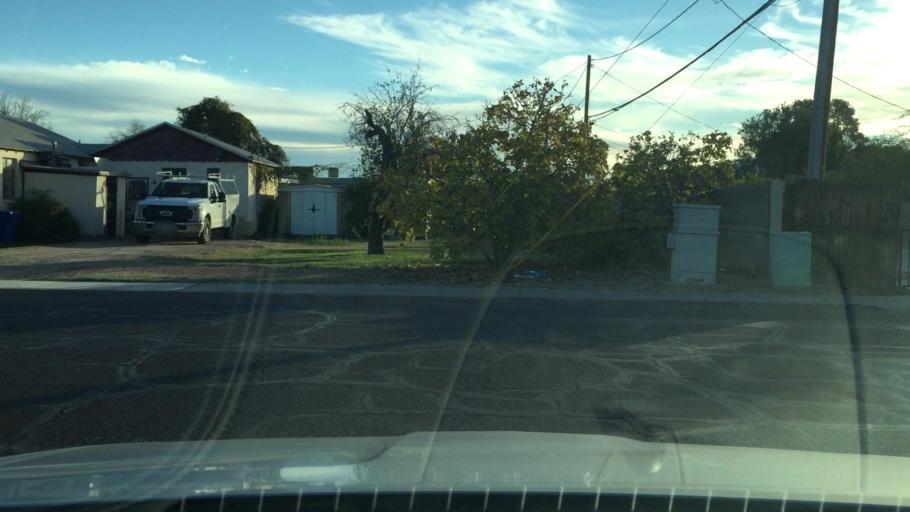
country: US
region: Arizona
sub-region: Maricopa County
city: Mesa
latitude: 33.4129
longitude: -111.8444
